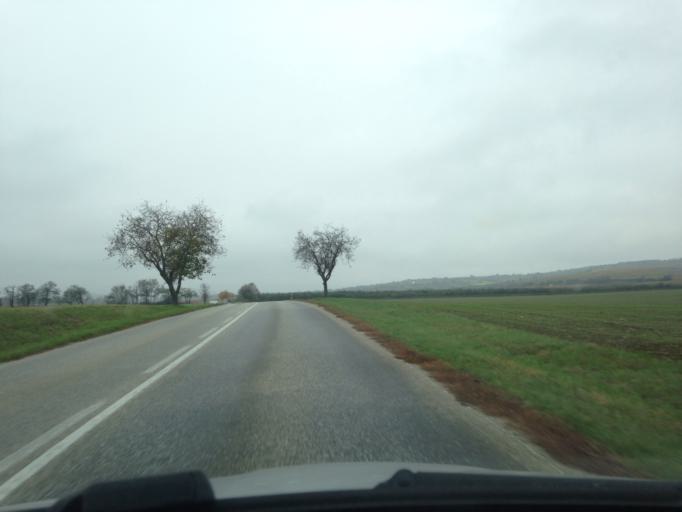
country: HU
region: Komarom-Esztergom
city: Nyergesujfalu
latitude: 47.8316
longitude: 18.5502
